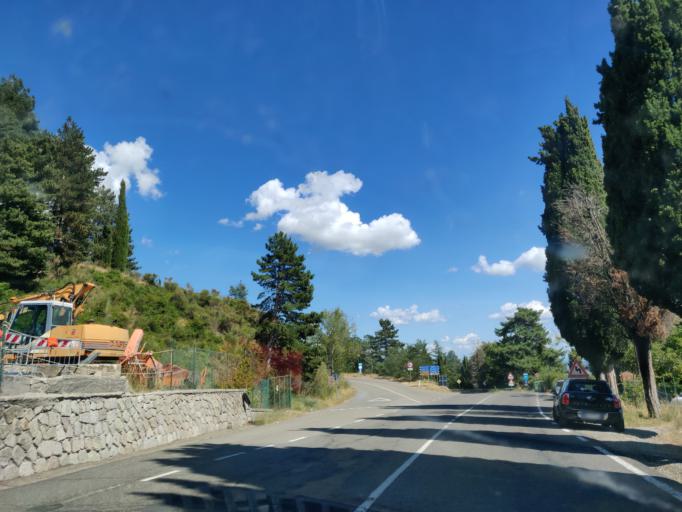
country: IT
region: Tuscany
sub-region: Provincia di Siena
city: Abbadia San Salvatore
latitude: 42.9094
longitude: 11.6723
